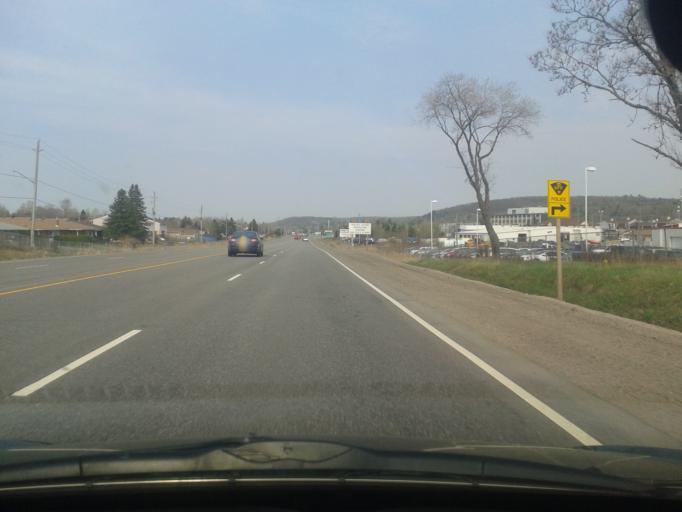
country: CA
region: Ontario
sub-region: Nipissing District
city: North Bay
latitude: 46.3309
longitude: -79.4773
